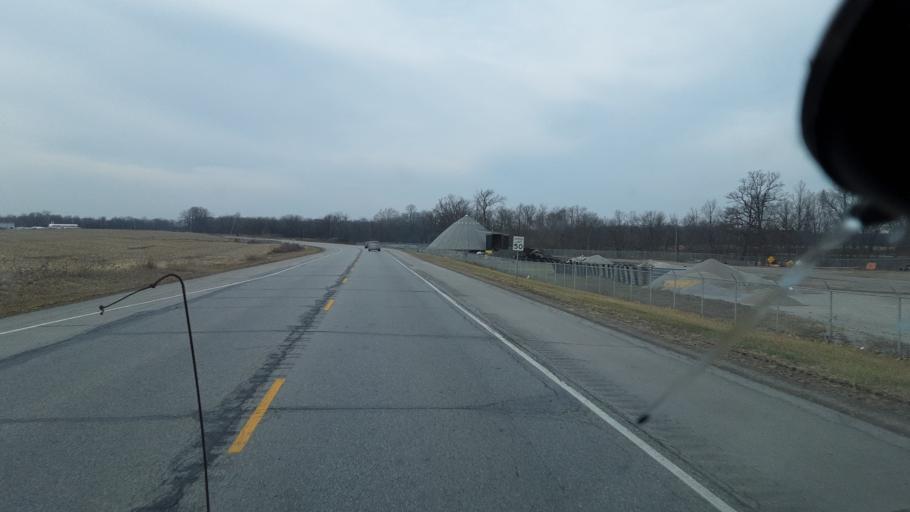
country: US
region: Indiana
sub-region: DeKalb County
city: Waterloo
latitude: 41.4373
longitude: -85.0353
